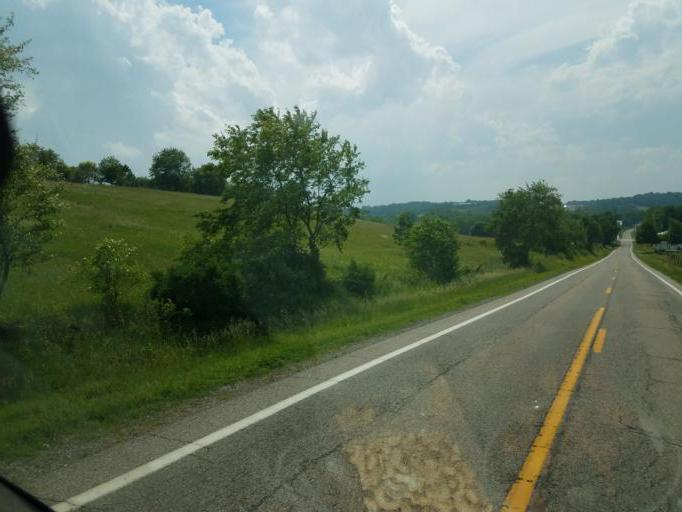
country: US
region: Ohio
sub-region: Knox County
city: Oak Hill
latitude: 40.2851
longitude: -82.2725
